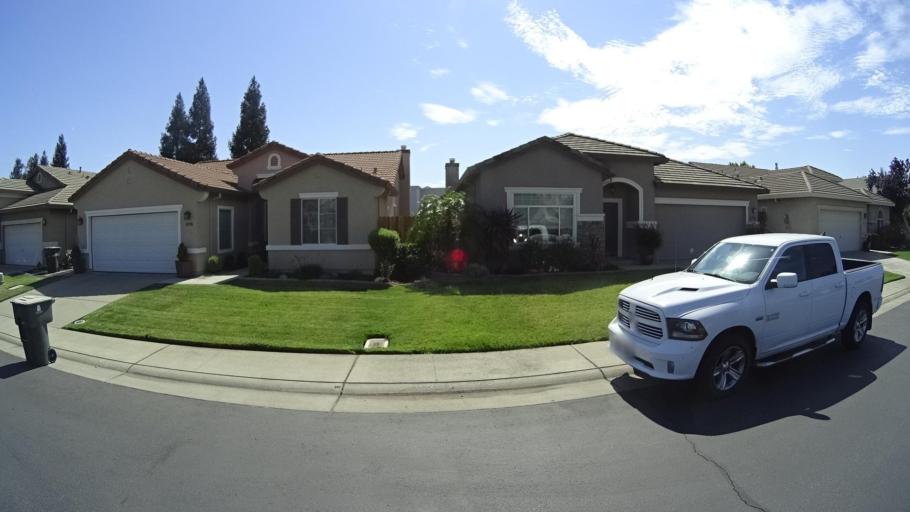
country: US
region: California
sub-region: Placer County
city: Roseville
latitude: 38.7976
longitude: -121.2887
